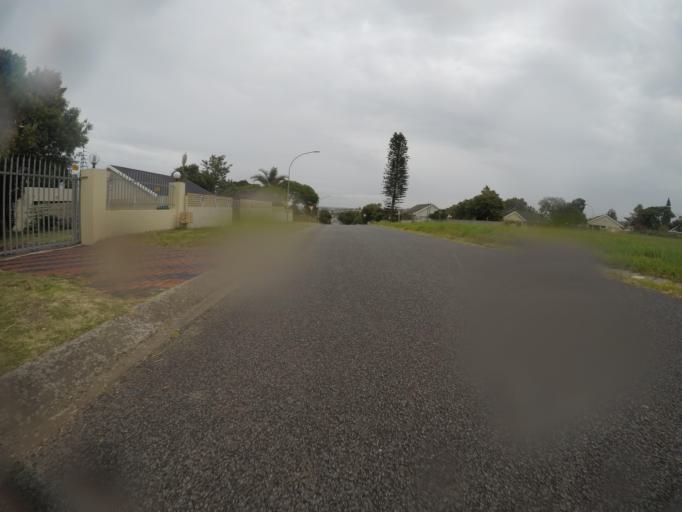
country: ZA
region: Eastern Cape
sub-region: Buffalo City Metropolitan Municipality
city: East London
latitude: -32.9942
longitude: 27.8512
